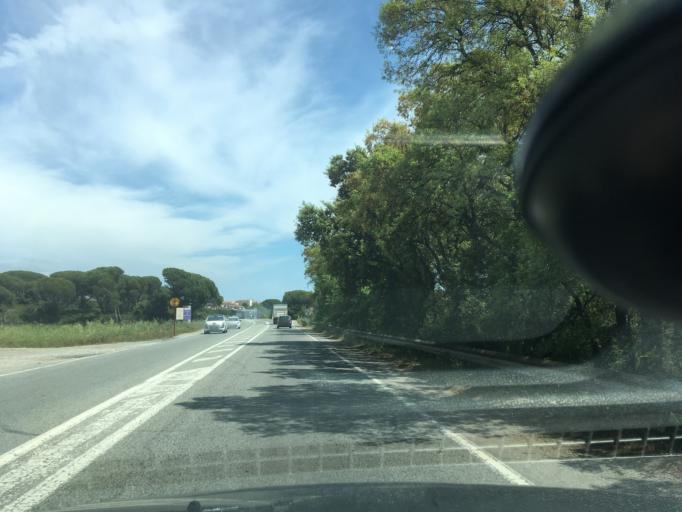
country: FR
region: Provence-Alpes-Cote d'Azur
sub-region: Departement du Var
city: Puget-sur-Argens
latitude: 43.4594
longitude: 6.6669
